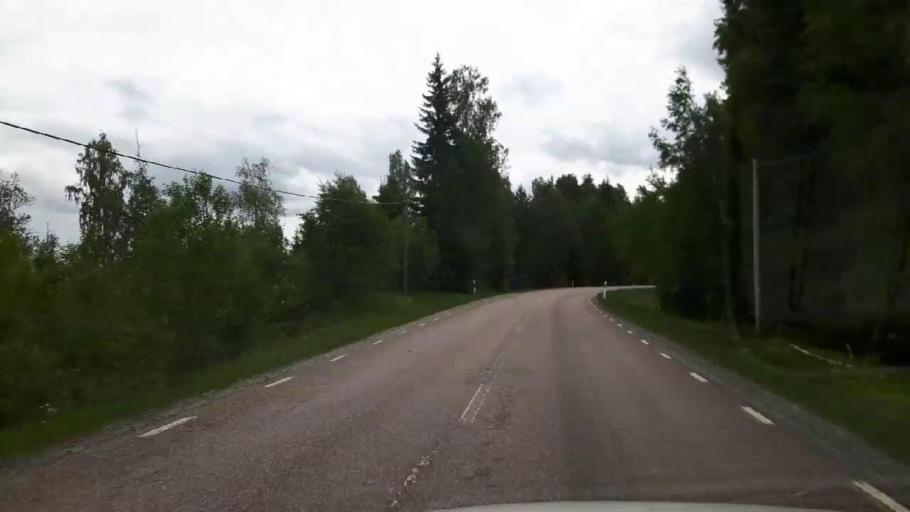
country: SE
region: Vaestmanland
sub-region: Fagersta Kommun
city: Fagersta
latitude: 59.9310
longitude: 15.8270
